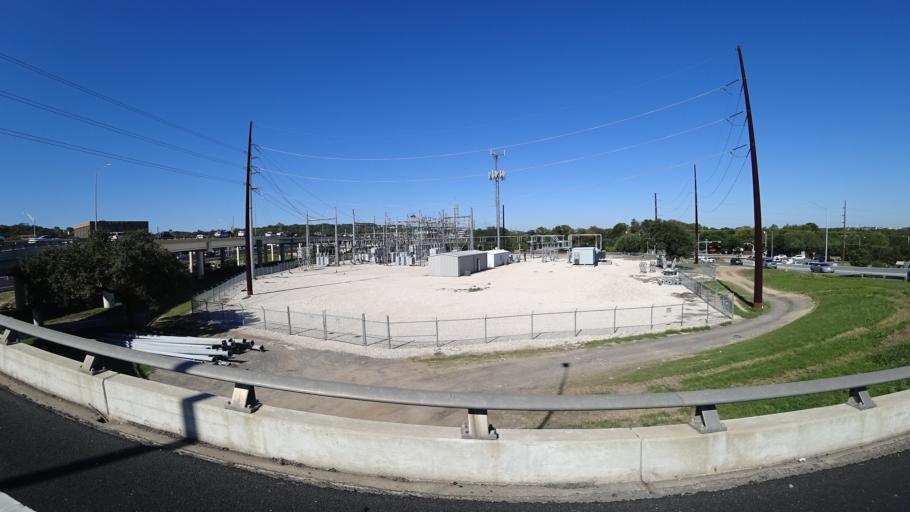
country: US
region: Texas
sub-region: Travis County
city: West Lake Hills
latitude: 30.3346
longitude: -97.7549
